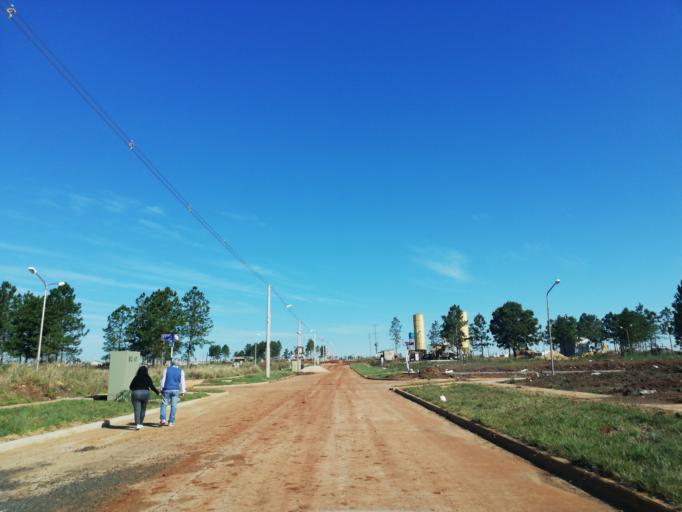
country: AR
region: Misiones
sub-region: Departamento de Capital
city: Posadas
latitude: -27.4048
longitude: -55.9918
